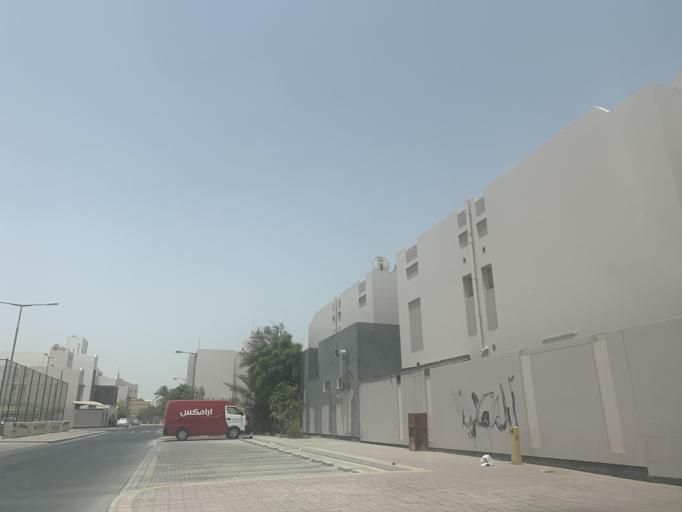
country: BH
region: Manama
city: Jidd Hafs
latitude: 26.2119
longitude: 50.5369
